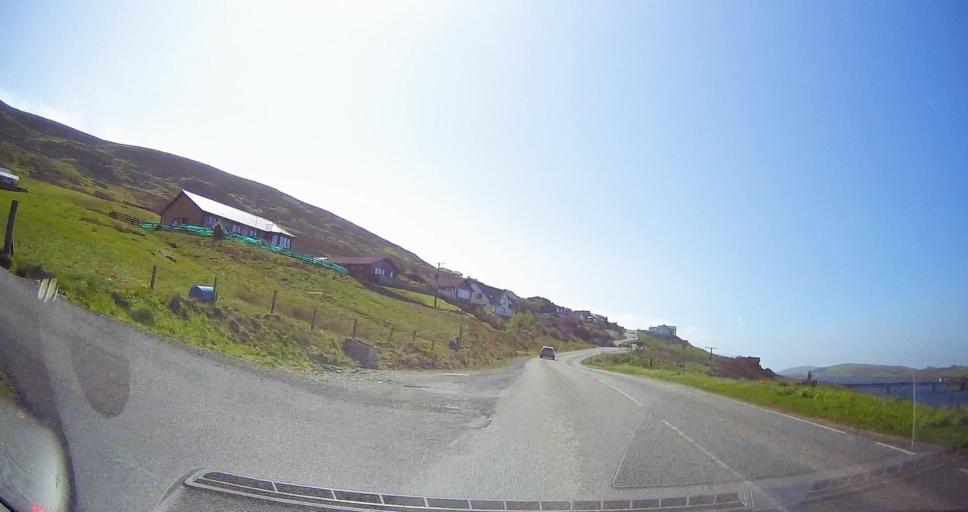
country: GB
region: Scotland
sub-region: Shetland Islands
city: Lerwick
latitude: 60.1334
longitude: -1.2673
